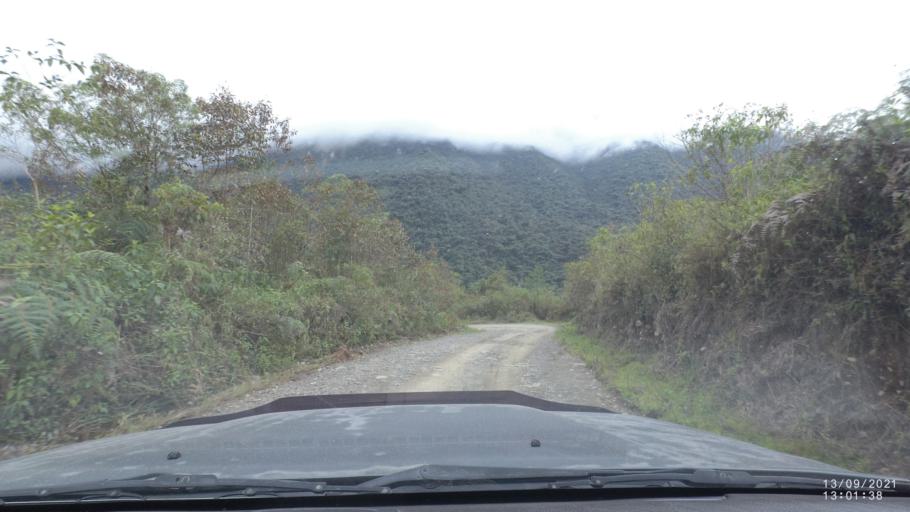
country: BO
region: Cochabamba
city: Colomi
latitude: -17.2313
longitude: -65.8183
